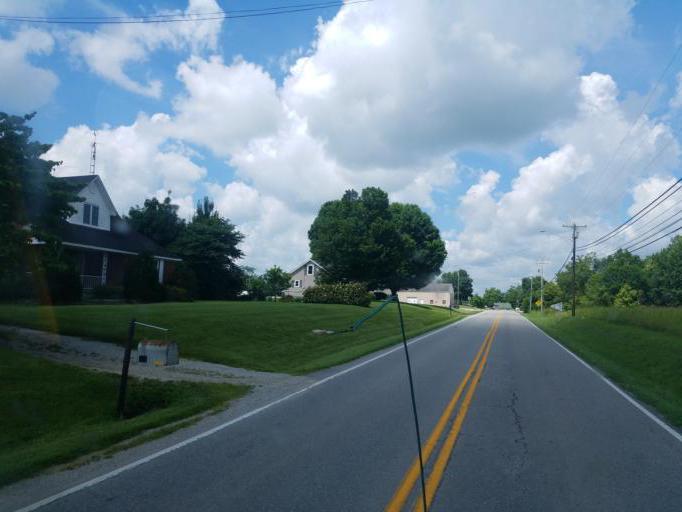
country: US
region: Kentucky
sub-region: Grayson County
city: Leitchfield
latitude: 37.4958
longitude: -86.2301
